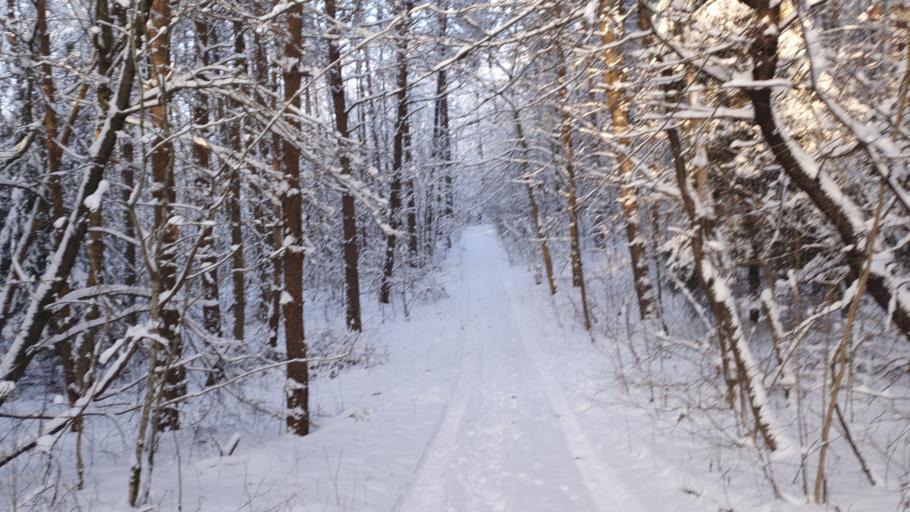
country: LT
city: Skaidiskes
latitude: 54.6426
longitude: 25.4167
